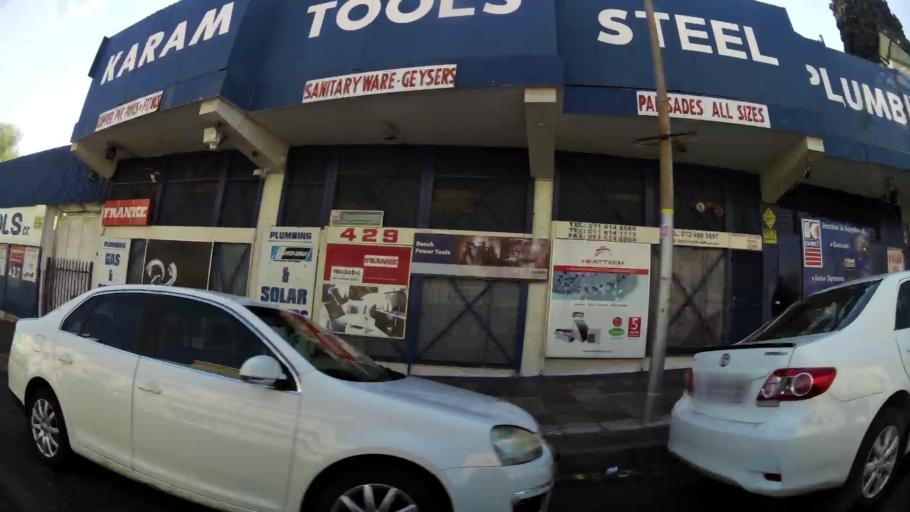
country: ZA
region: Gauteng
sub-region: City of Johannesburg Metropolitan Municipality
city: Johannesburg
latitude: -26.2018
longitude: 28.0732
